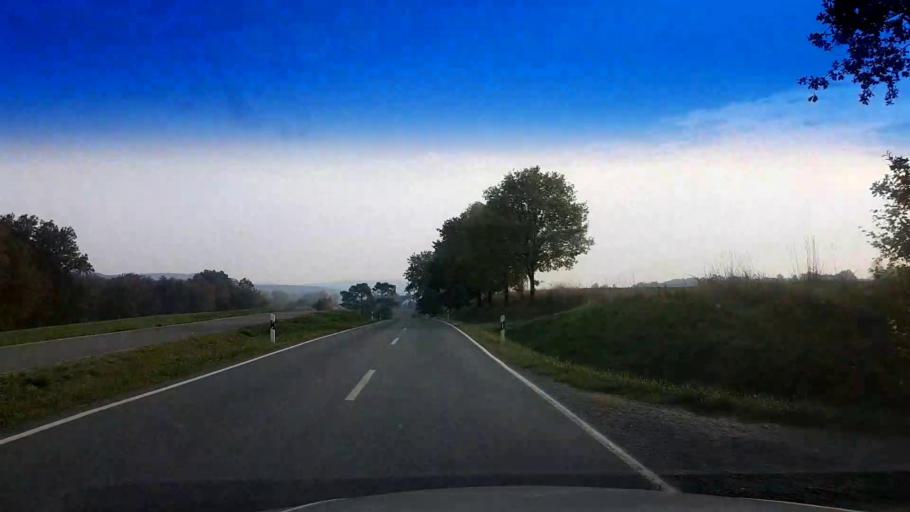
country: DE
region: Bavaria
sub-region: Upper Franconia
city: Altenkunstadt
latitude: 50.1164
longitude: 11.2869
